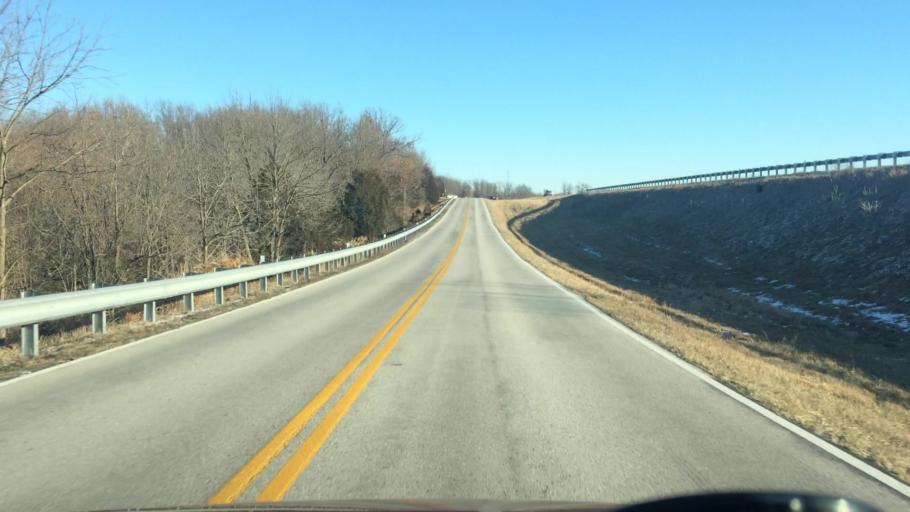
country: US
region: Missouri
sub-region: Greene County
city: Strafford
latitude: 37.2796
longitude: -93.0457
